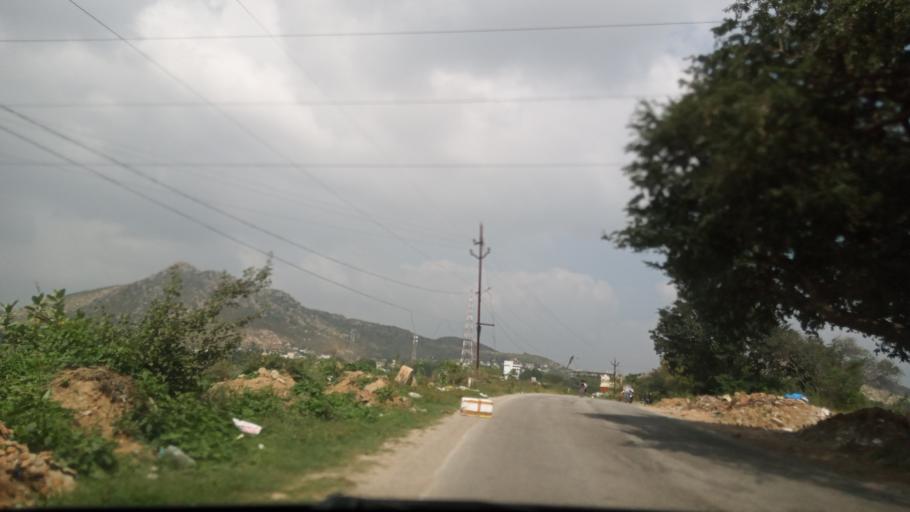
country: IN
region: Andhra Pradesh
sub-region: Chittoor
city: Madanapalle
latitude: 13.5742
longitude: 78.5181
